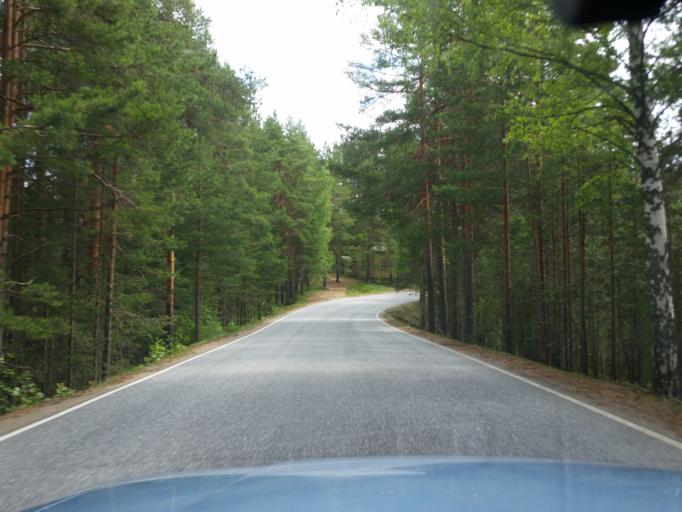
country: FI
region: Southern Savonia
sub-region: Savonlinna
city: Sulkava
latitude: 61.7735
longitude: 28.4315
